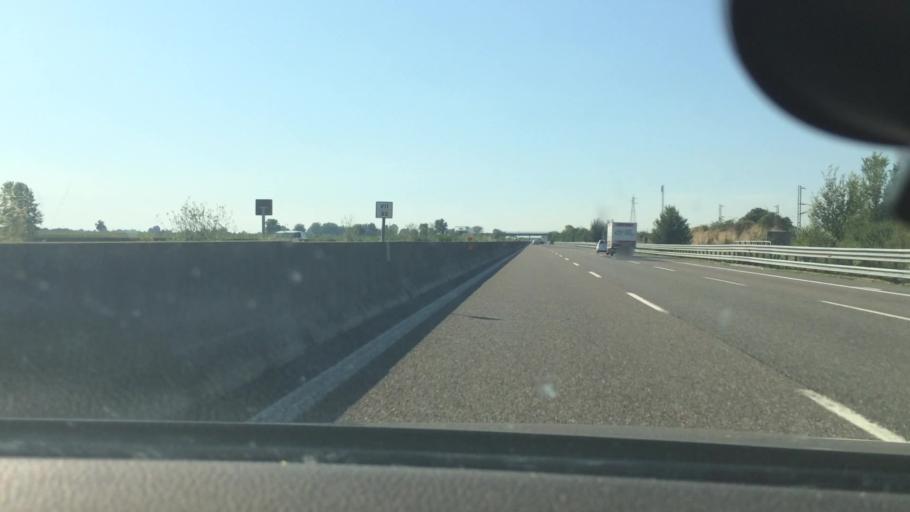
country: IT
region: Lombardy
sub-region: Provincia di Lodi
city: Livraga
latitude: 45.2106
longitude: 9.5363
